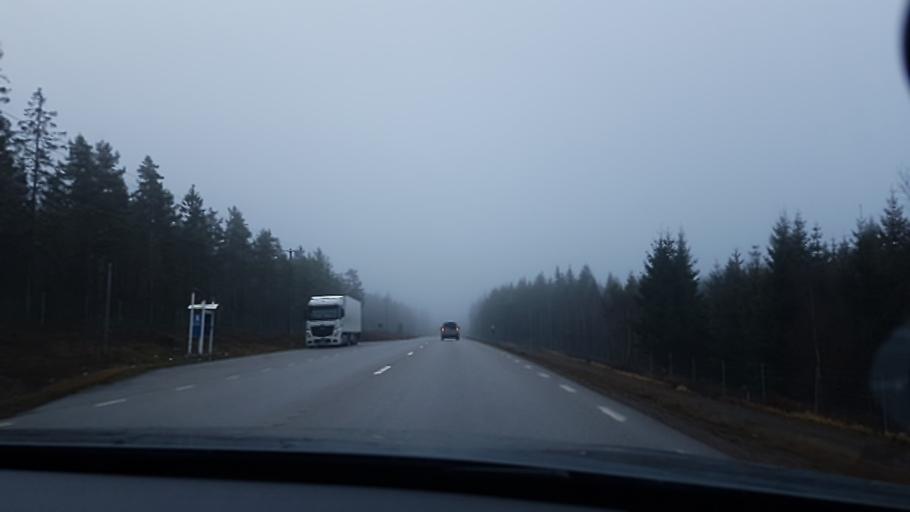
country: SE
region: Vaestra Goetaland
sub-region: Gullspangs Kommun
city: Gullspang
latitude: 58.9274
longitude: 14.0329
